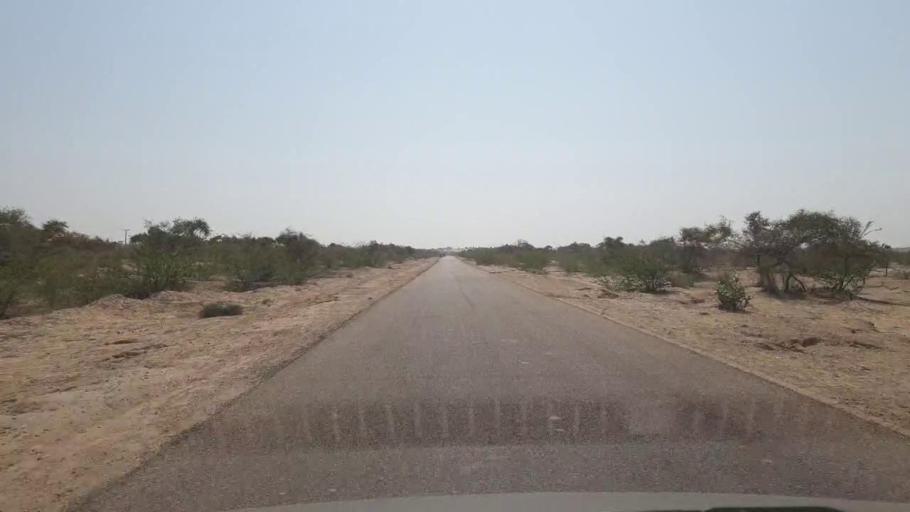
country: PK
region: Sindh
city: Chor
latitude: 25.5939
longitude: 70.1827
